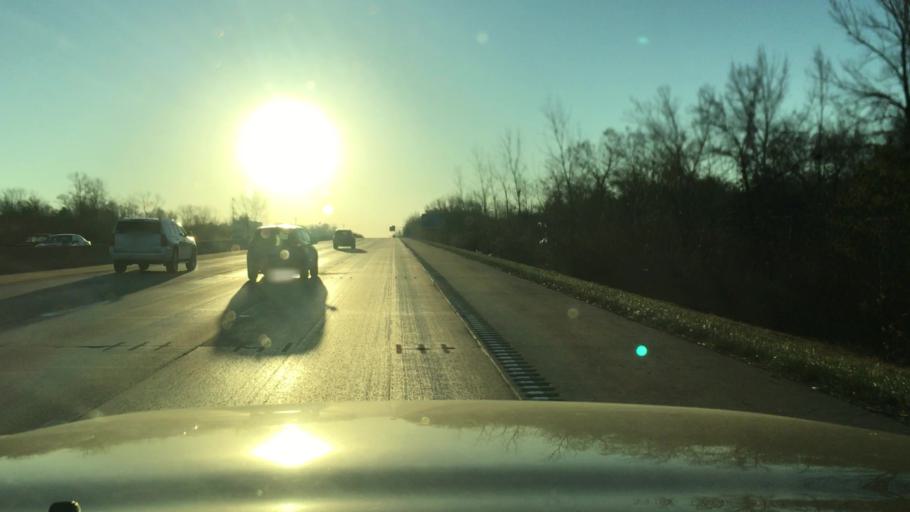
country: US
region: Missouri
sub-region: Saint Charles County
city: Saint Charles
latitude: 38.8174
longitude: -90.4963
